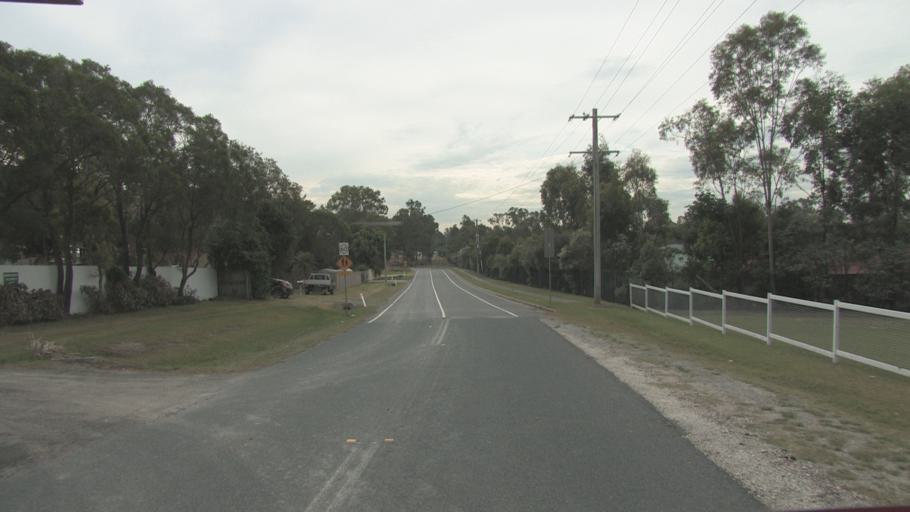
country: AU
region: Queensland
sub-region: Logan
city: Waterford West
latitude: -27.7049
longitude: 153.1487
